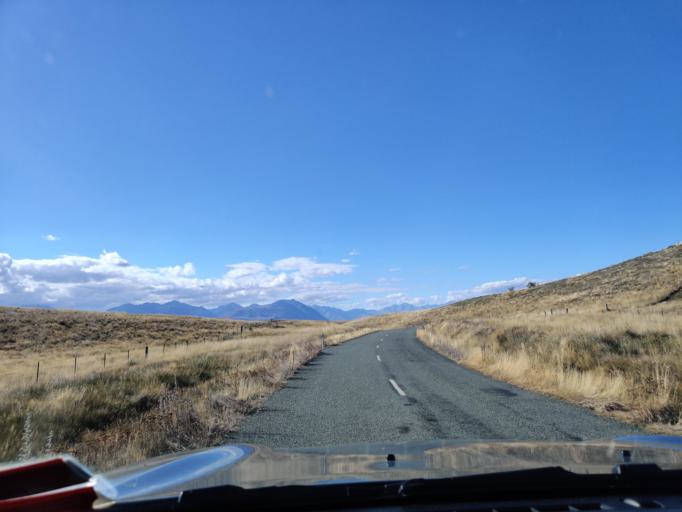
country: NZ
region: Canterbury
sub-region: Timaru District
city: Pleasant Point
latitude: -43.9769
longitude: 170.4638
